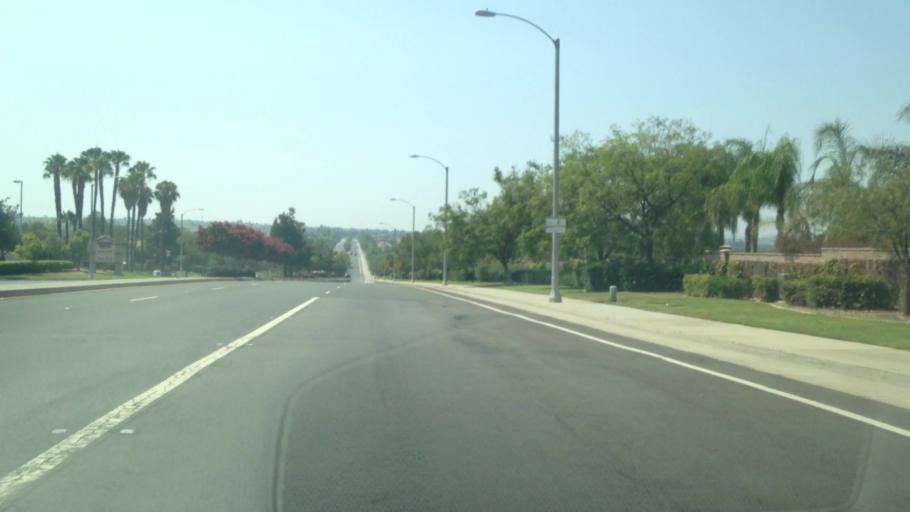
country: US
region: California
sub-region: Riverside County
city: Woodcrest
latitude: 33.9149
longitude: -117.3311
